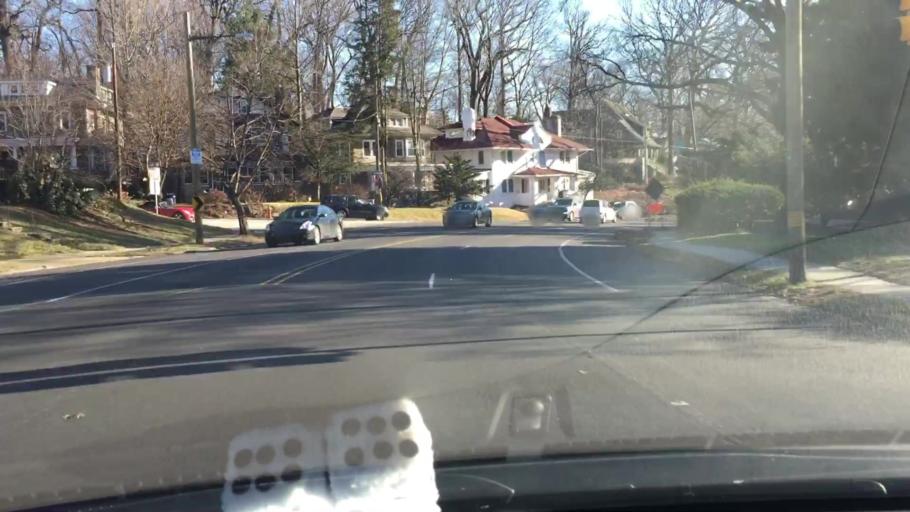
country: US
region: Pennsylvania
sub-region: Montgomery County
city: Wyndmoor
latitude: 40.0429
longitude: -75.1935
